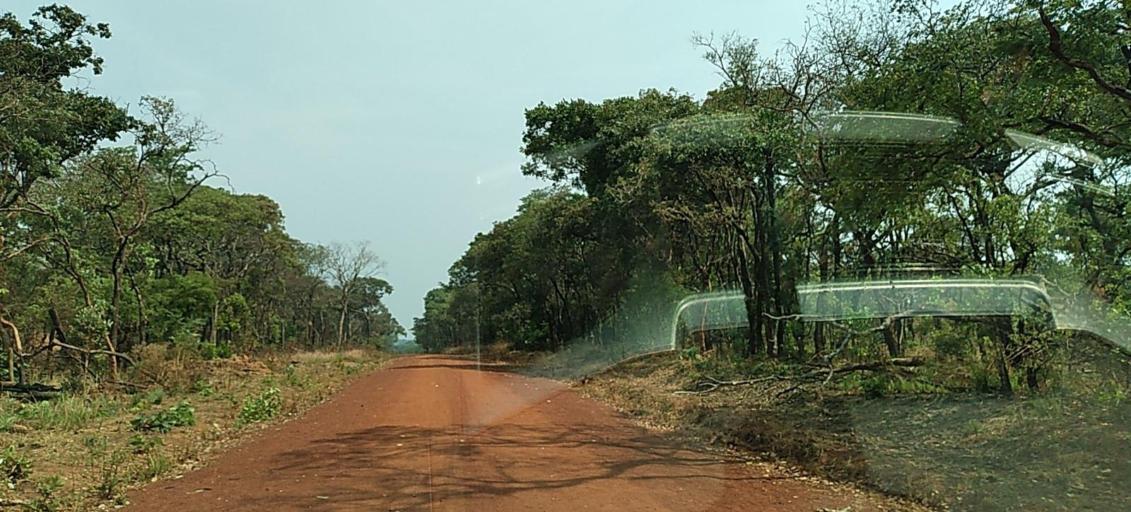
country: ZM
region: North-Western
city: Kansanshi
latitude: -12.0075
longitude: 26.8446
